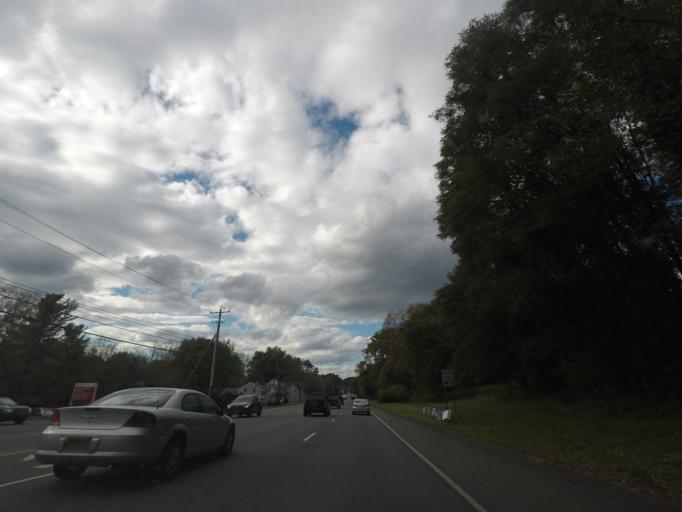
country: US
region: New York
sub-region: Albany County
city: Westmere
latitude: 42.7013
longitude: -73.9045
